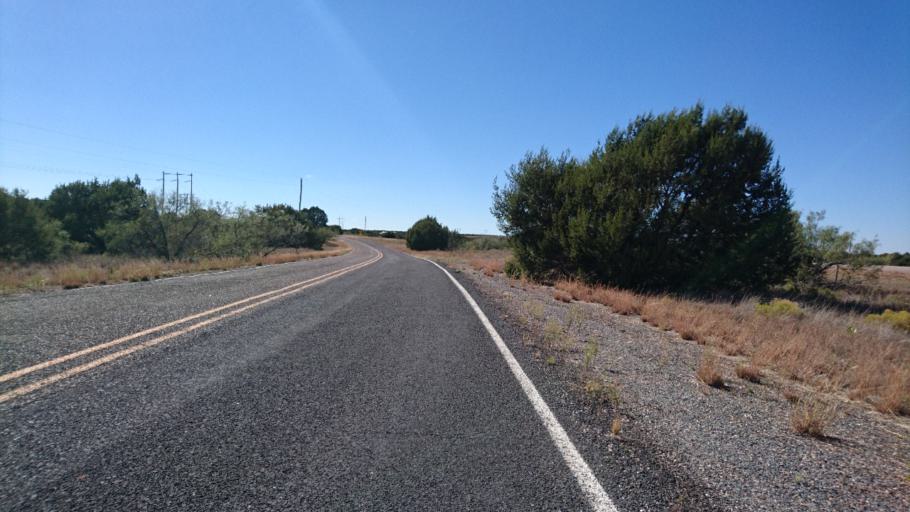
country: US
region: New Mexico
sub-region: Quay County
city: Tucumcari
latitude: 35.0675
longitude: -104.1732
